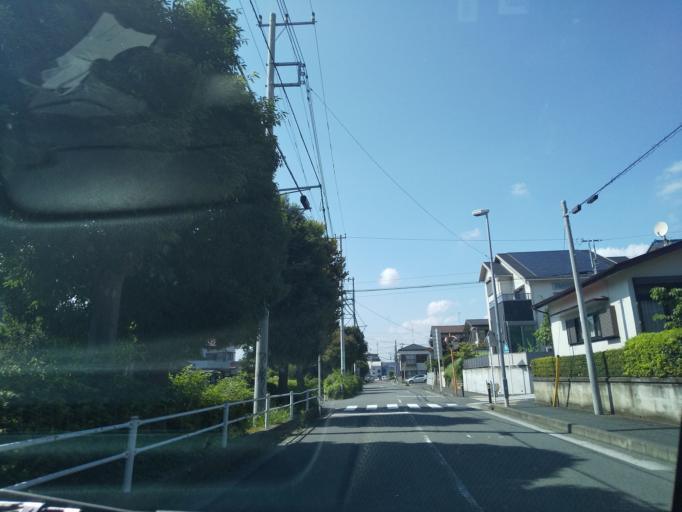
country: JP
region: Kanagawa
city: Zama
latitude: 35.4606
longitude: 139.4165
